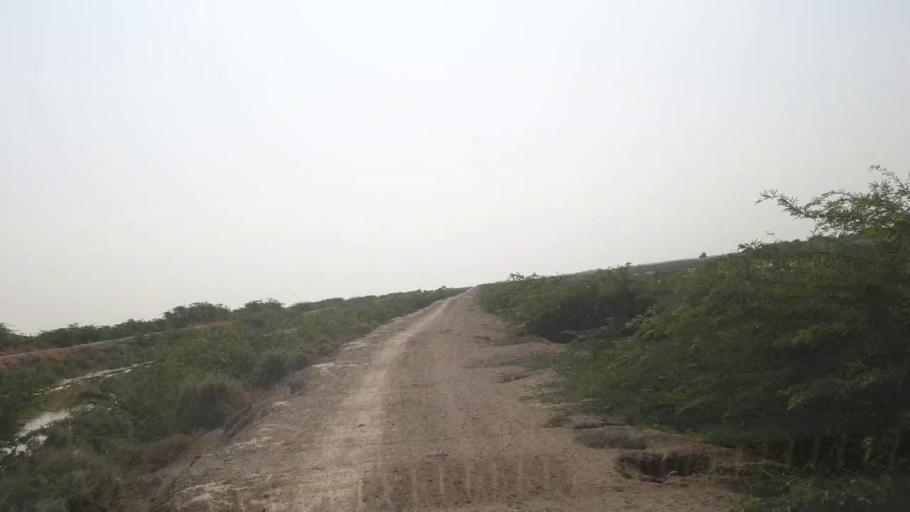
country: PK
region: Sindh
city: Kadhan
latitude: 24.3923
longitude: 68.9029
